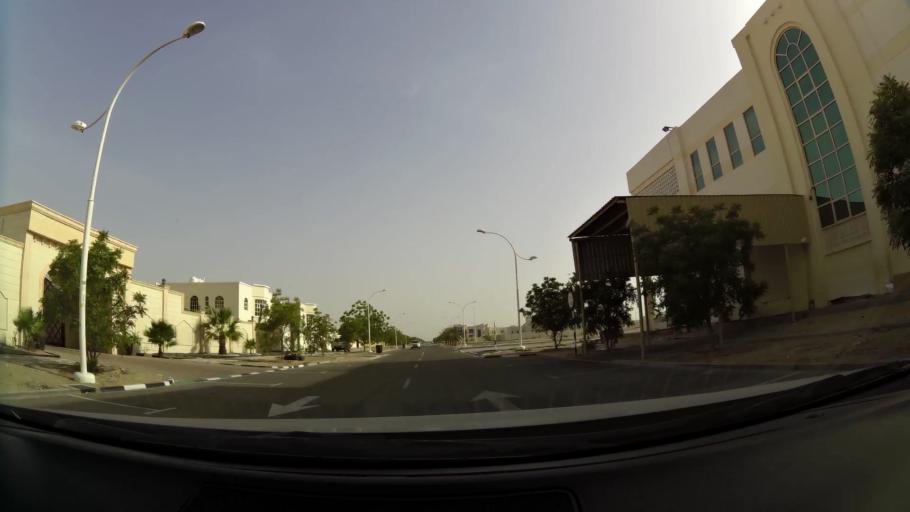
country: AE
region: Abu Dhabi
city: Al Ain
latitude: 24.1513
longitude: 55.7196
